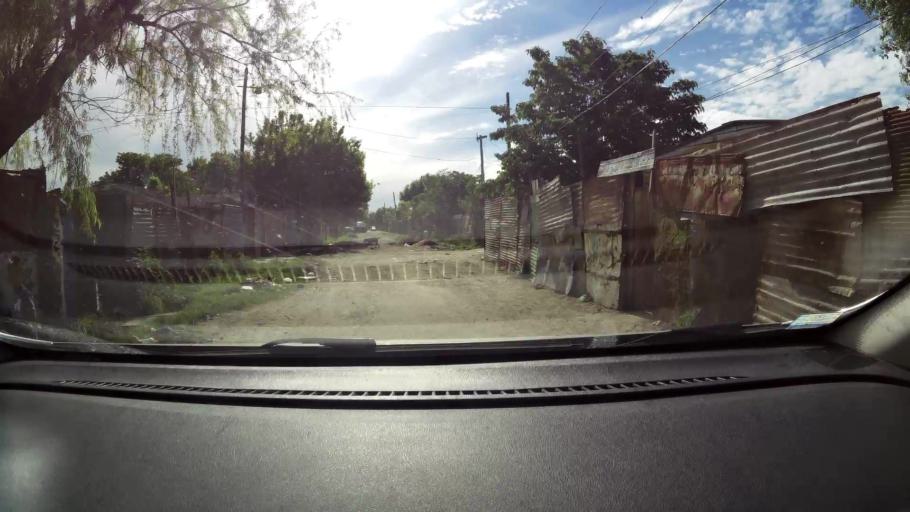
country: AR
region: Santa Fe
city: Granadero Baigorria
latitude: -32.9102
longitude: -60.7035
